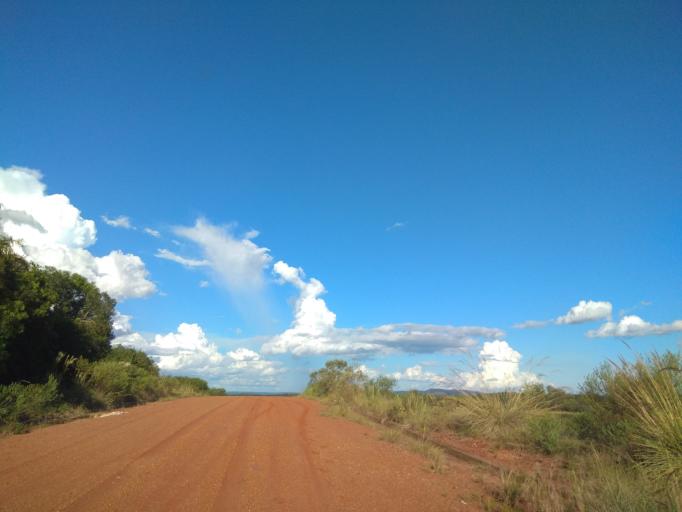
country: AR
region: Misiones
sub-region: Departamento de Candelaria
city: Candelaria
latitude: -27.4890
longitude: -55.7548
